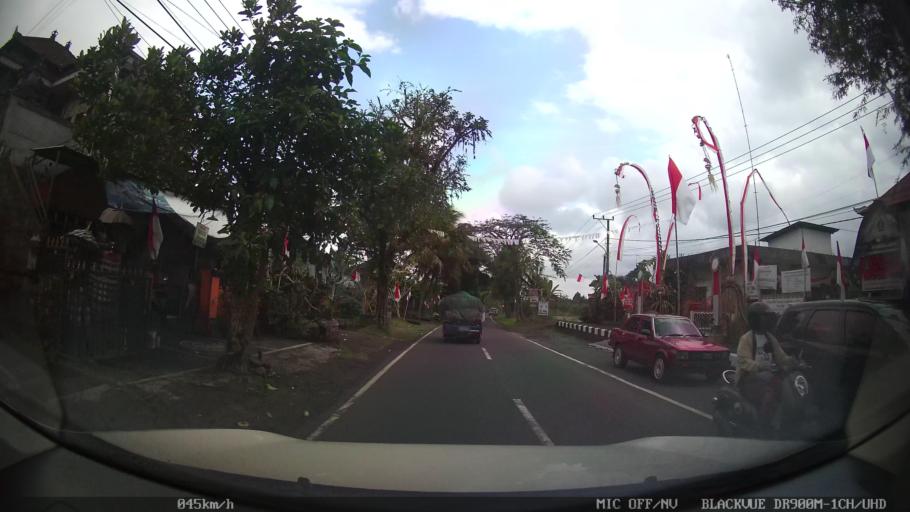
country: ID
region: Bali
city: Pohgending Kawan
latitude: -8.4372
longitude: 115.1427
